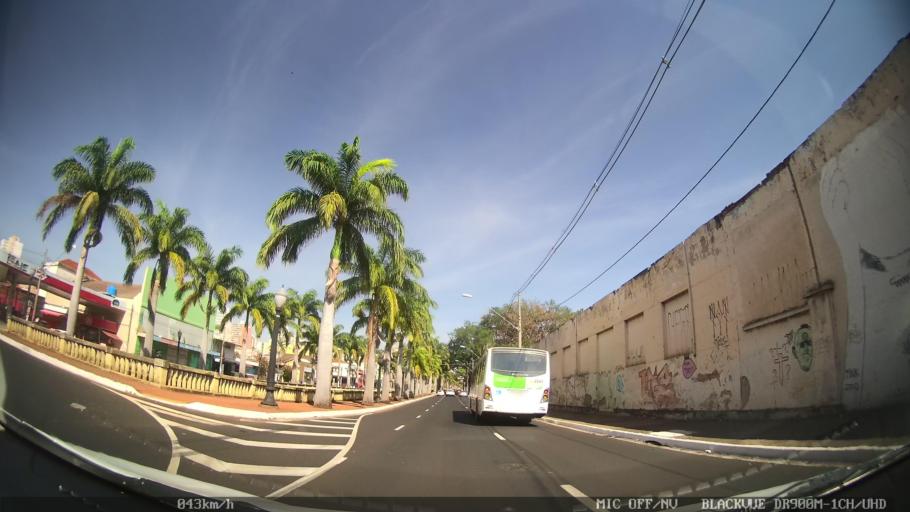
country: BR
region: Sao Paulo
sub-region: Ribeirao Preto
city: Ribeirao Preto
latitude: -21.1706
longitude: -47.8120
